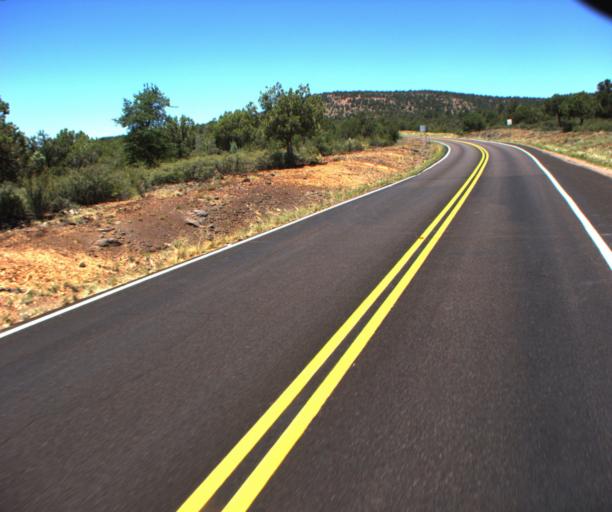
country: US
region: Arizona
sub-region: Gila County
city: Pine
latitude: 34.3383
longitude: -111.4219
